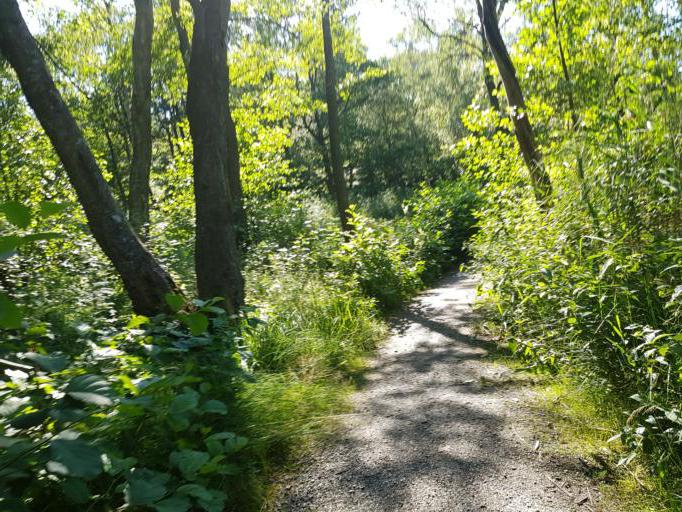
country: SE
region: Vaestra Goetaland
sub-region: Partille Kommun
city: Furulund
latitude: 57.7050
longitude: 12.1359
